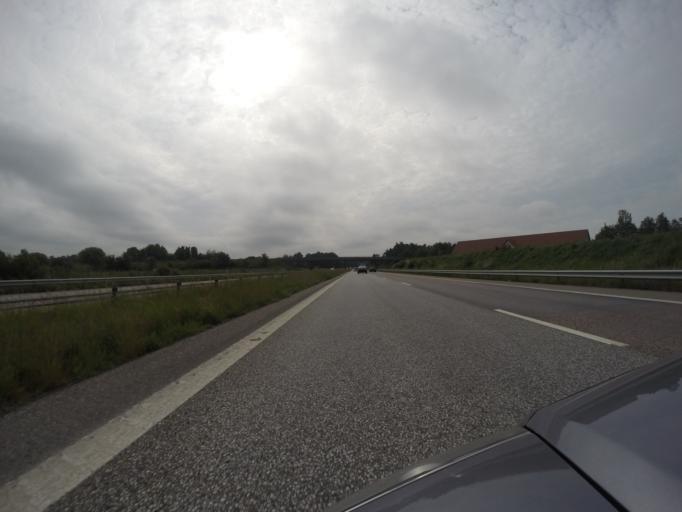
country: SE
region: Skane
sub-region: Landskrona
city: Asmundtorp
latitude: 55.8422
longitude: 12.9140
